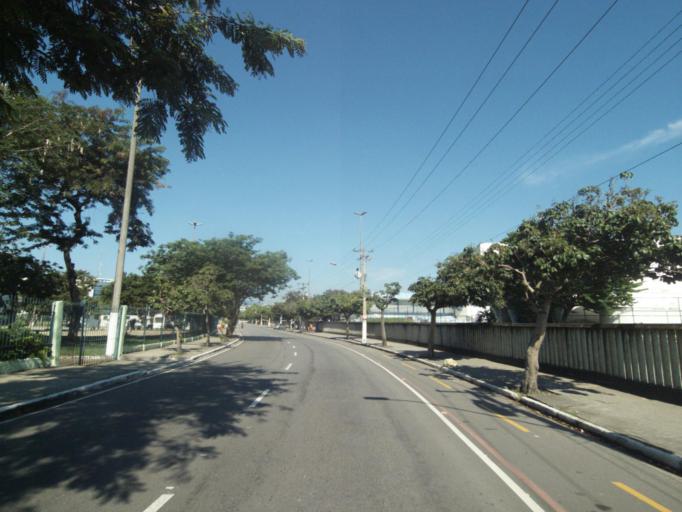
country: BR
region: Rio de Janeiro
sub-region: Niteroi
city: Niteroi
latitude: -22.8963
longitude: -43.1279
